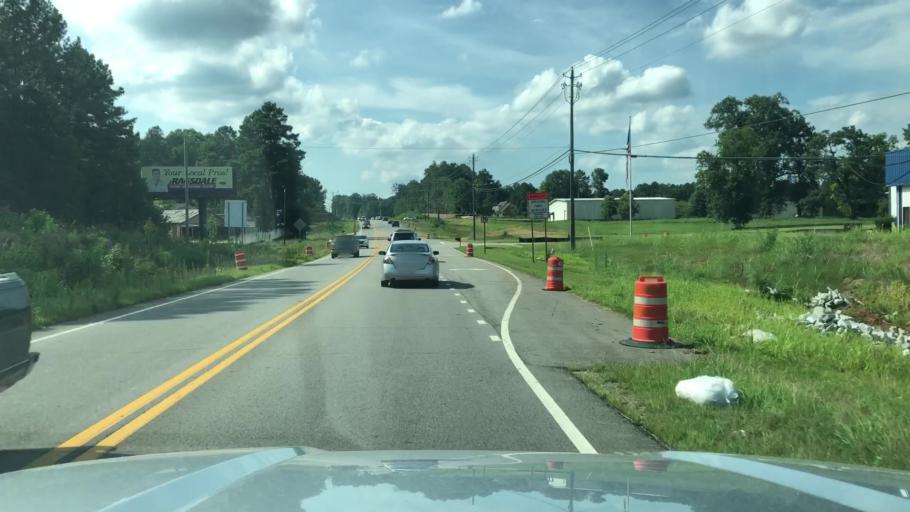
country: US
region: Georgia
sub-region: Douglas County
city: Douglasville
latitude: 33.7886
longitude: -84.7508
